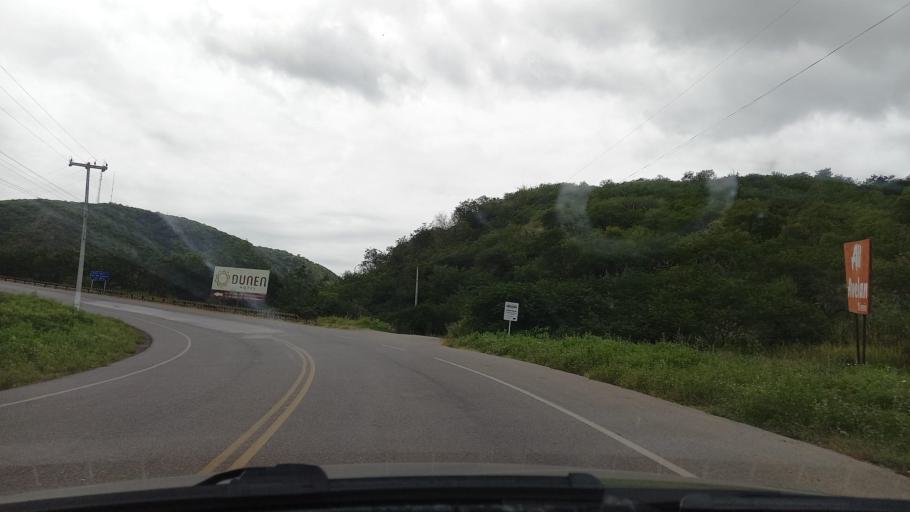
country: BR
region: Sergipe
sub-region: Caninde De Sao Francisco
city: Caninde de Sao Francisco
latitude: -9.6383
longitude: -37.7727
